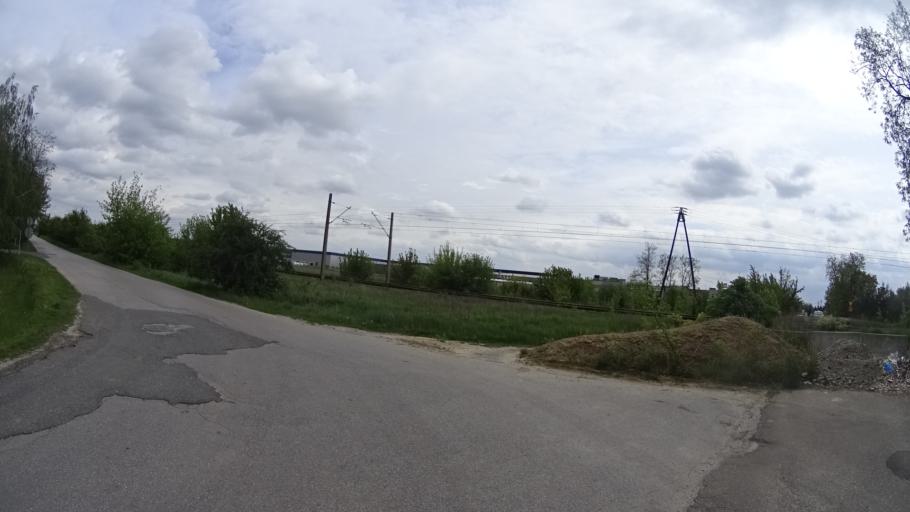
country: PL
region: Masovian Voivodeship
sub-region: Powiat pruszkowski
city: Piastow
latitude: 52.2068
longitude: 20.8369
